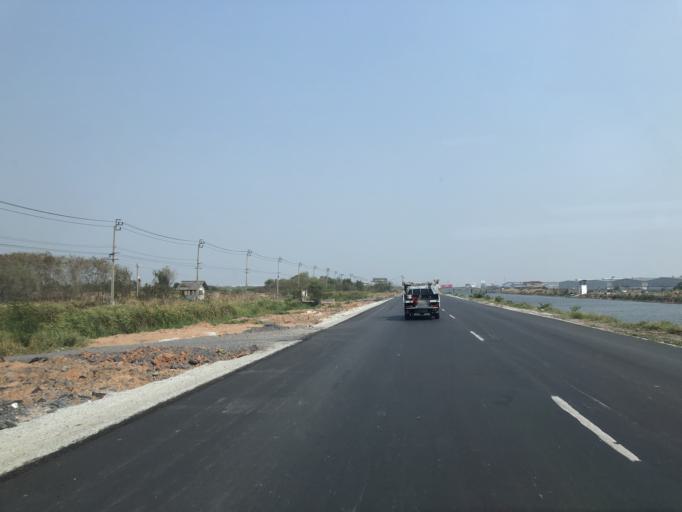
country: TH
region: Samut Prakan
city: Bang Bo District
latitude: 13.5494
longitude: 100.7522
